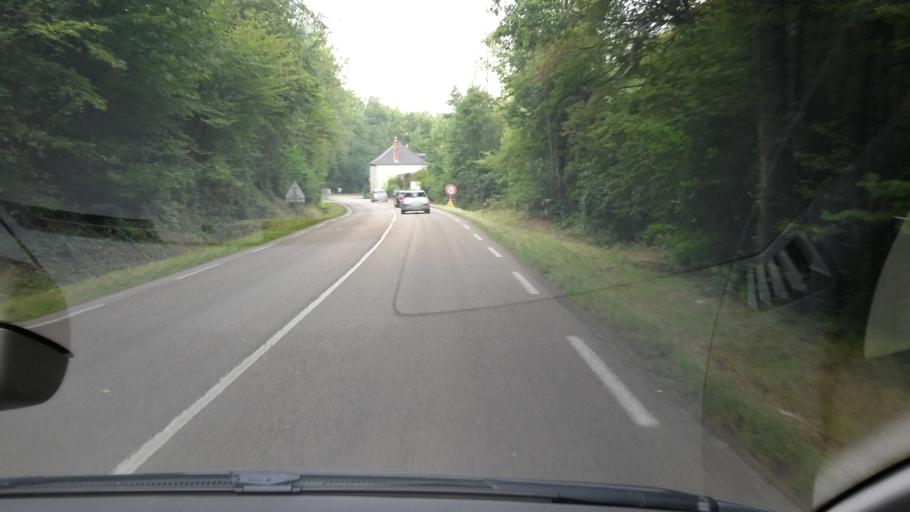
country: FR
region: Champagne-Ardenne
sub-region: Departement de la Marne
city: Verzenay
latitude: 49.1455
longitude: 4.0965
